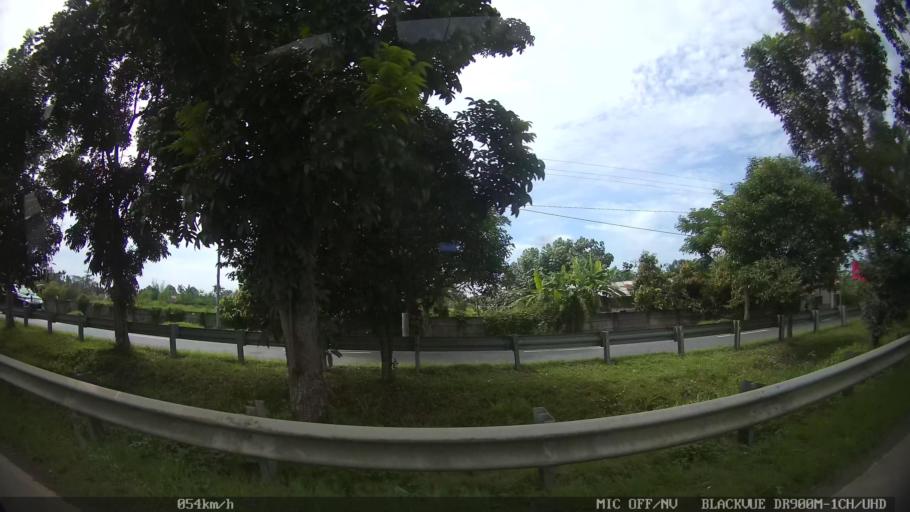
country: ID
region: North Sumatra
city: Percut
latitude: 3.5974
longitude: 98.8095
